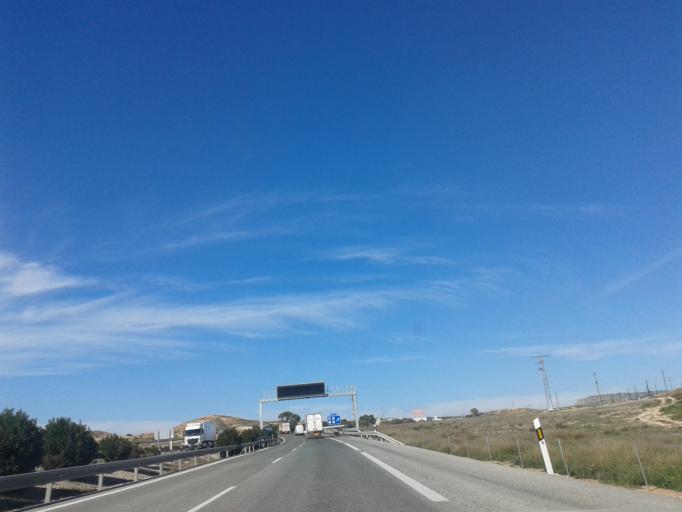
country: ES
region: Castille-La Mancha
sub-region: Provincia de Albacete
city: Caudete
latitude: 38.7227
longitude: -0.9342
